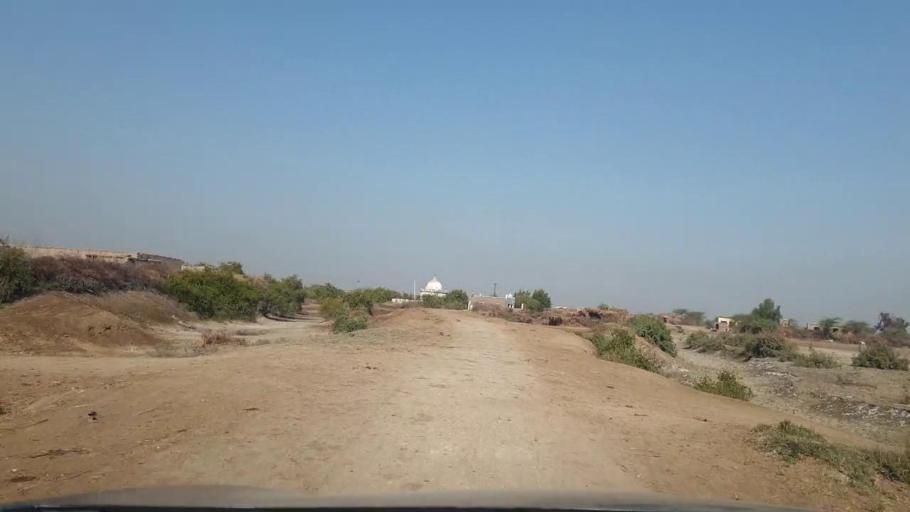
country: PK
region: Sindh
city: Mirpur Khas
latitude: 25.6276
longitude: 68.8914
